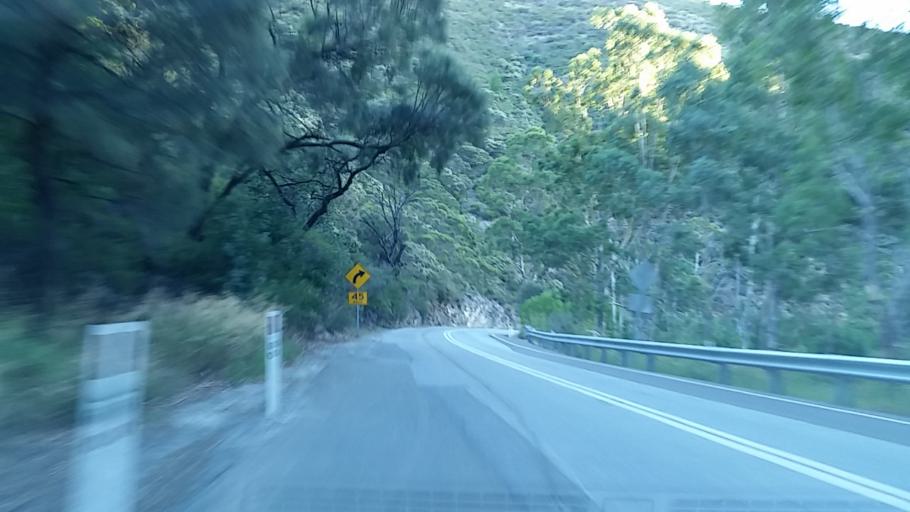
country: AU
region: South Australia
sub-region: Campbelltown
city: Athelstone
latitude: -34.8597
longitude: 138.7402
